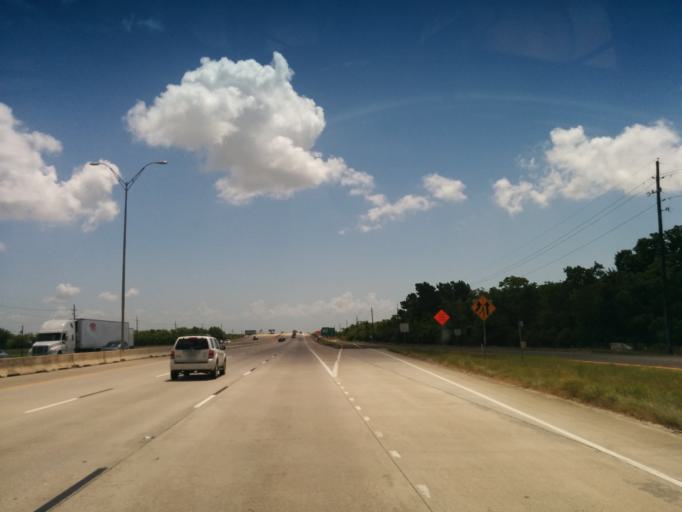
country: US
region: Texas
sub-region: Chambers County
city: Mont Belvieu
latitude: 29.8238
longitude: -94.8724
